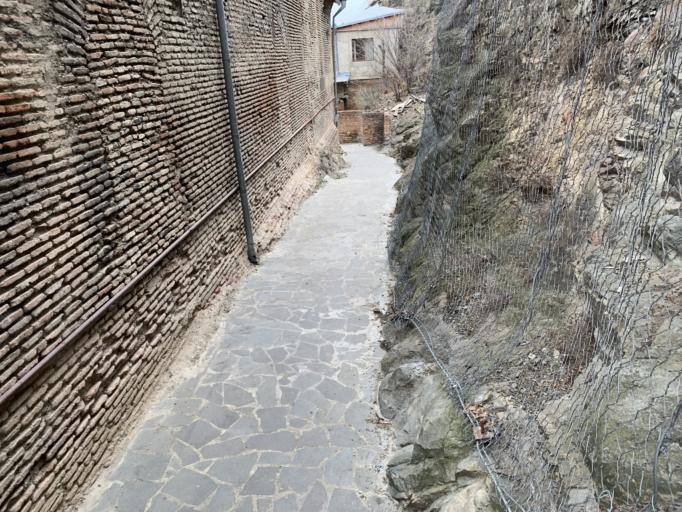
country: GE
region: T'bilisi
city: Tbilisi
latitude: 41.6888
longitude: 44.8044
